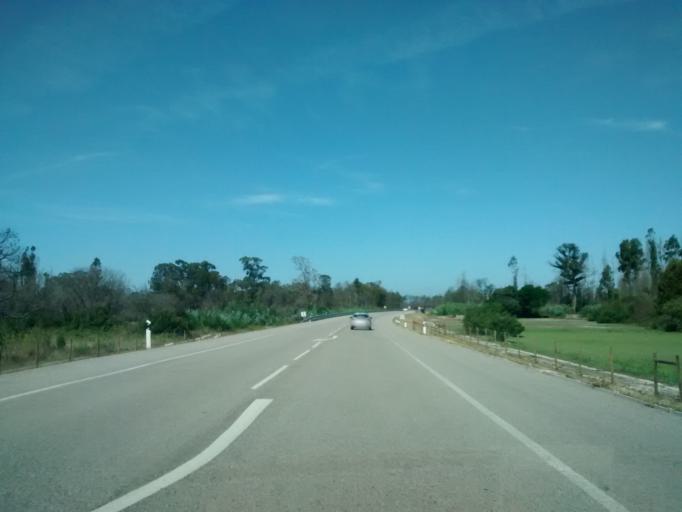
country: PT
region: Coimbra
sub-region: Mira
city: Mira
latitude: 40.4494
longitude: -8.7500
